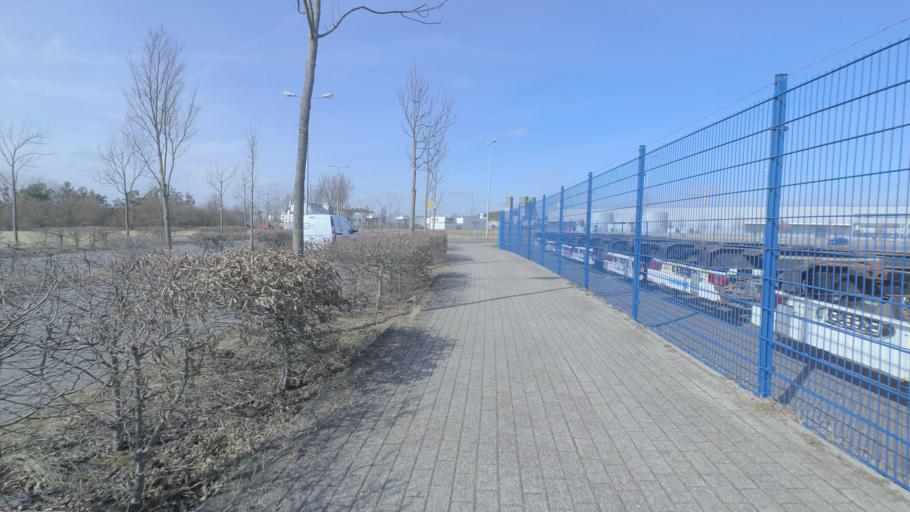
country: DE
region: Brandenburg
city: Ludwigsfelde
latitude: 52.2979
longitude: 13.2806
